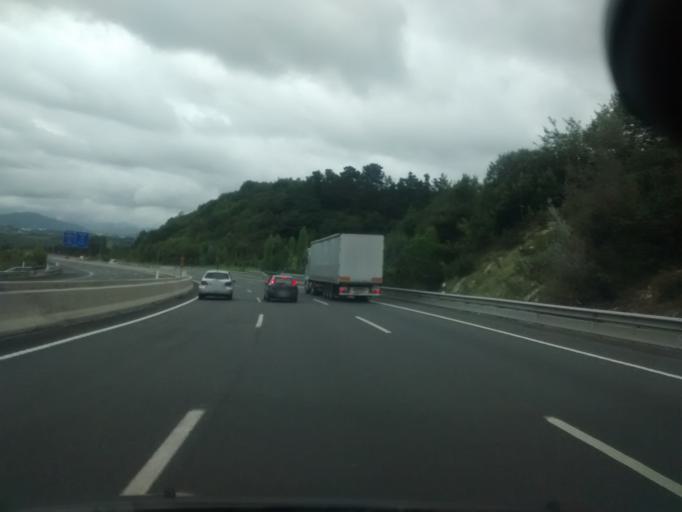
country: ES
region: Basque Country
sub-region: Provincia de Guipuzcoa
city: Usurbil
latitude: 43.2941
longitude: -2.0512
